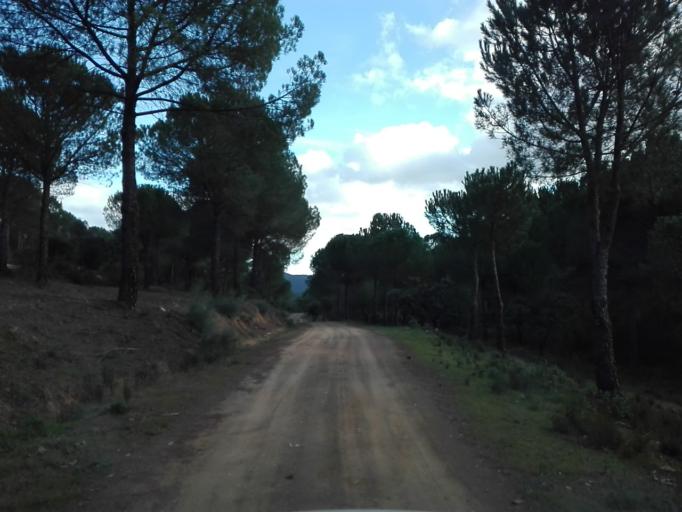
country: ES
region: Extremadura
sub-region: Provincia de Badajoz
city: Trasierra
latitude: 38.1801
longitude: -5.9780
